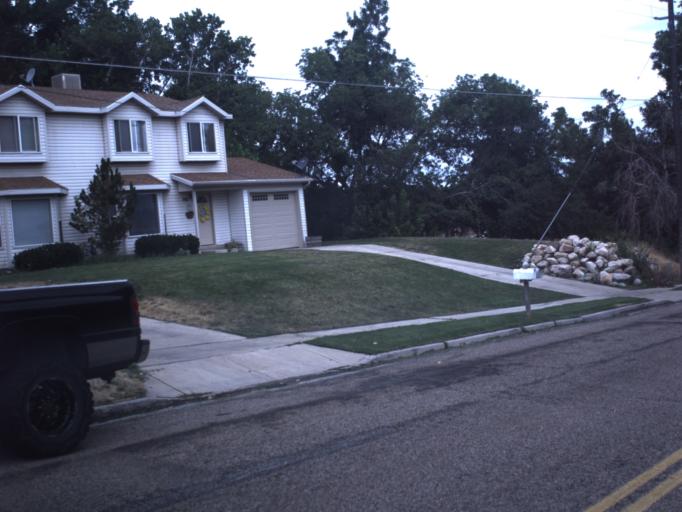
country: US
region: Utah
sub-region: Weber County
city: Riverdale
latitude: 41.1645
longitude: -112.0080
